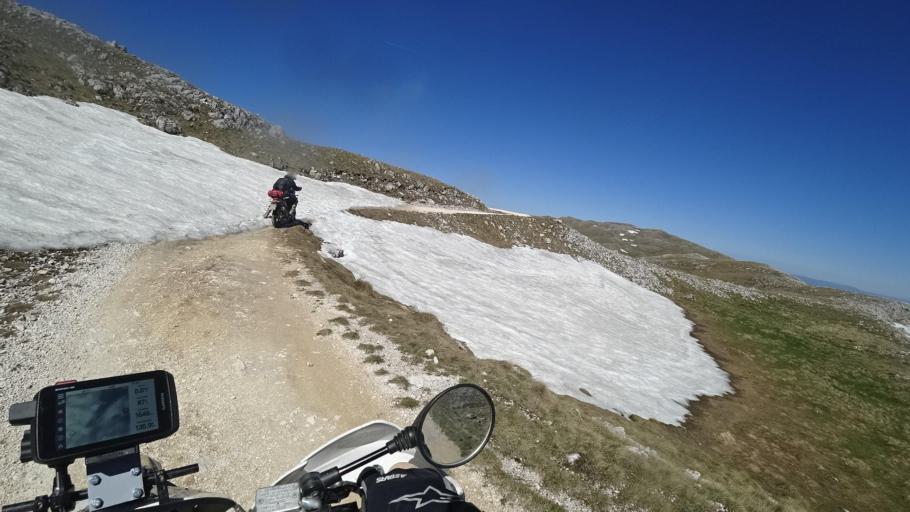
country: BA
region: Federation of Bosnia and Herzegovina
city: Travnik
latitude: 44.2854
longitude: 17.6378
